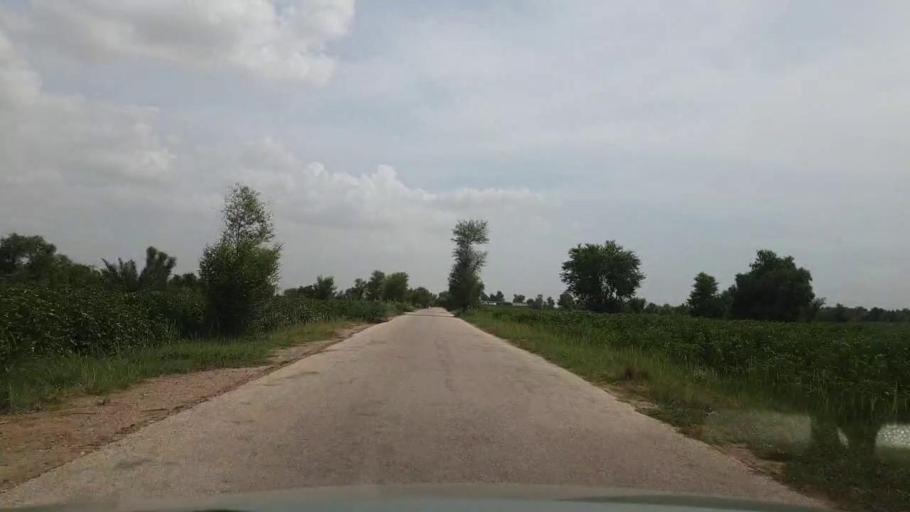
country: PK
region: Sindh
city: Kot Diji
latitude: 27.1399
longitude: 69.0281
